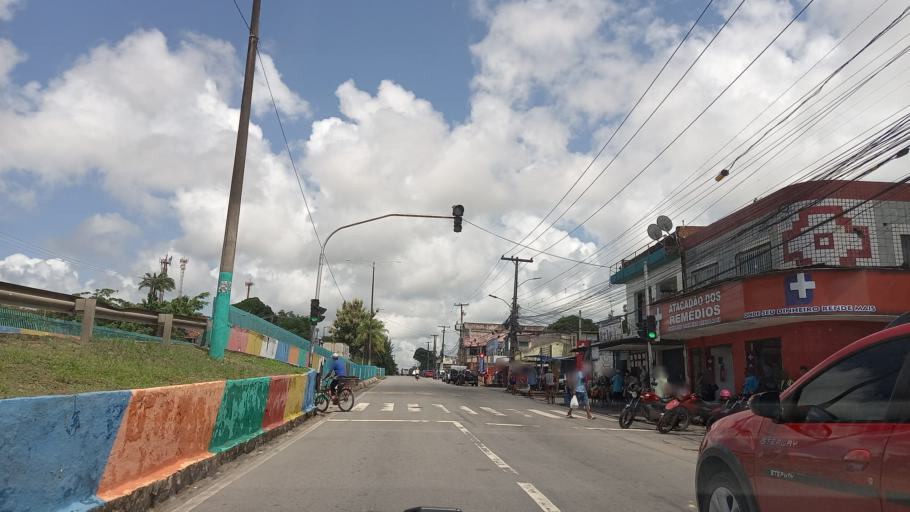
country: BR
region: Pernambuco
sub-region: Jaboatao Dos Guararapes
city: Jaboatao
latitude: -8.2363
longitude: -34.9816
